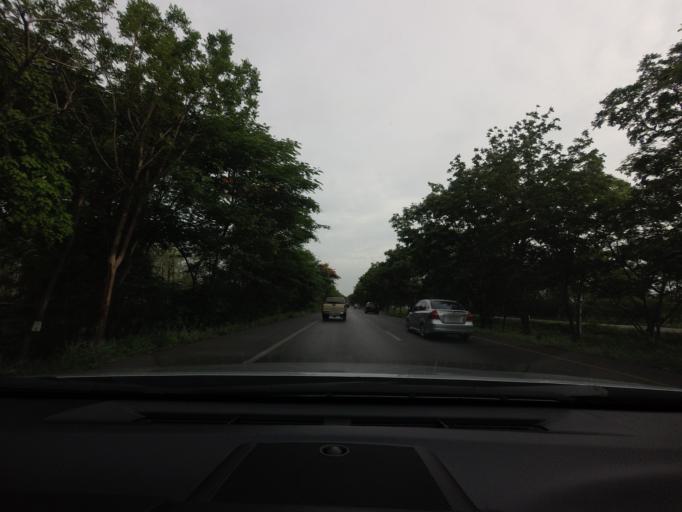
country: TH
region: Phetchaburi
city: Cha-am
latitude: 12.7836
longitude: 99.9384
